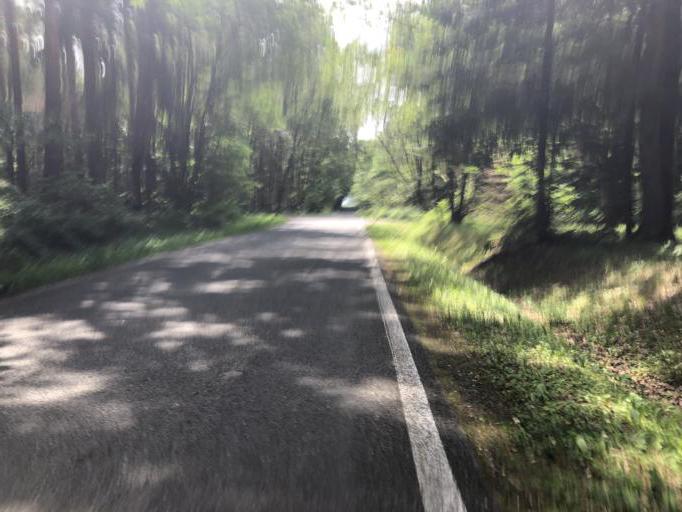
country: DE
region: Bavaria
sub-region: Regierungsbezirk Mittelfranken
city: Obermichelbach
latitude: 49.5720
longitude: 10.9340
